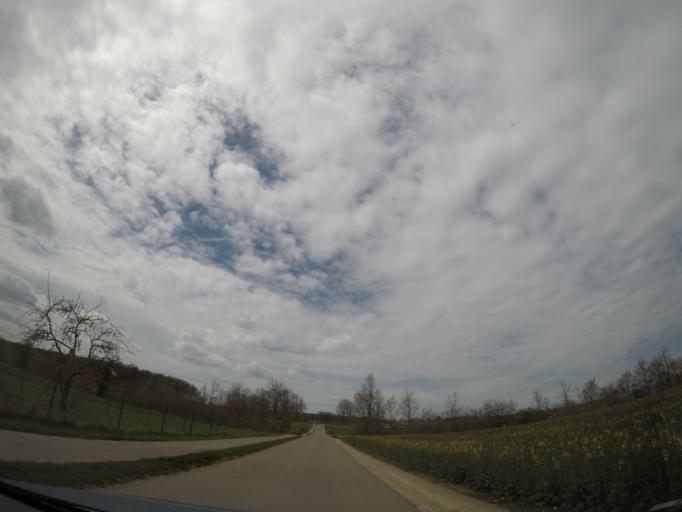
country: DE
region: Baden-Wuerttemberg
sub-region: Tuebingen Region
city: Laichingen
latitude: 48.4805
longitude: 9.6896
